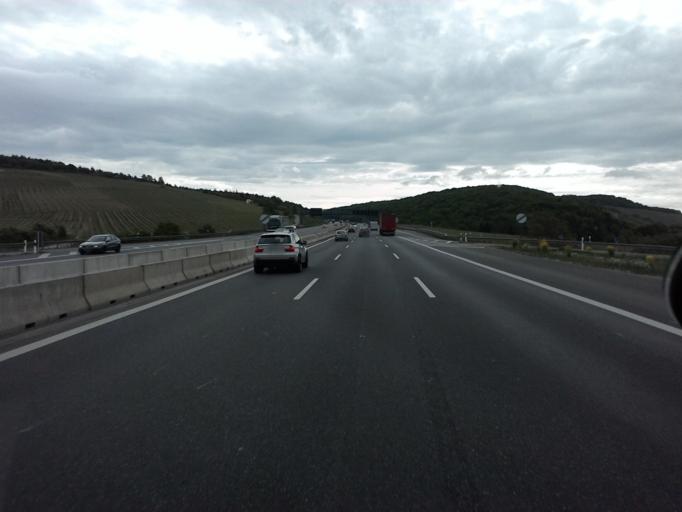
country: DE
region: Bavaria
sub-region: Regierungsbezirk Unterfranken
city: Eibelstadt
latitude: 49.7391
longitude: 9.9960
